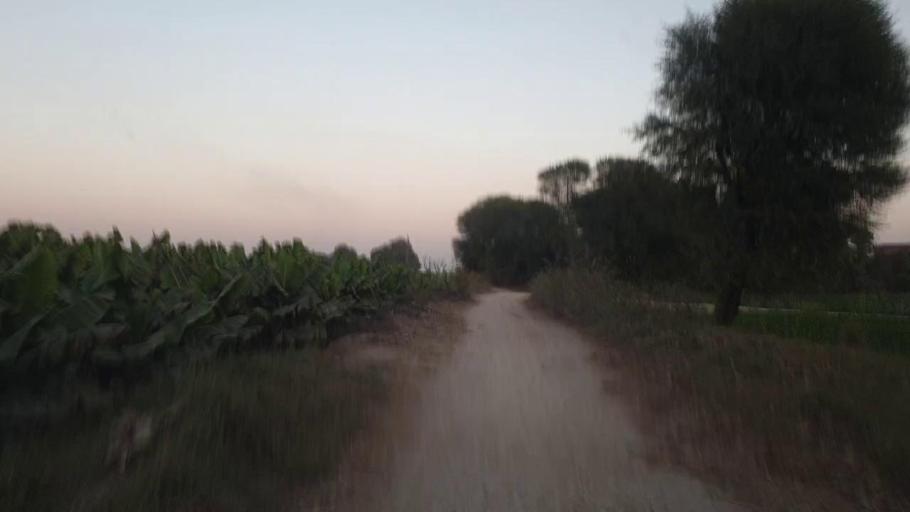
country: PK
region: Sindh
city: Chambar
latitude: 25.3413
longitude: 68.7559
